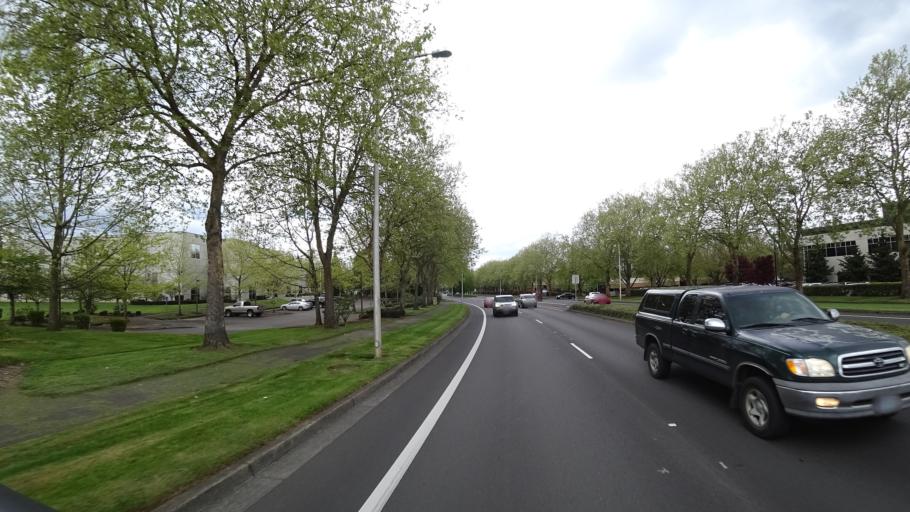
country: US
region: Oregon
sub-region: Washington County
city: Rockcreek
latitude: 45.5460
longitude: -122.8948
